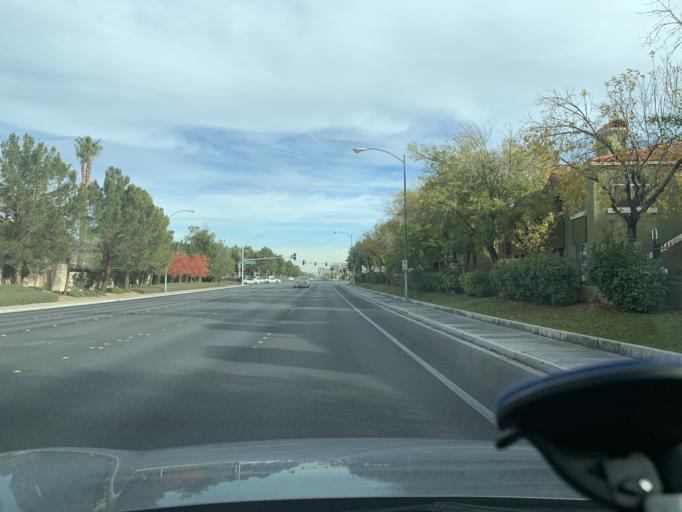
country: US
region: Nevada
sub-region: Clark County
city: Spring Valley
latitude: 36.0924
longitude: -115.2446
